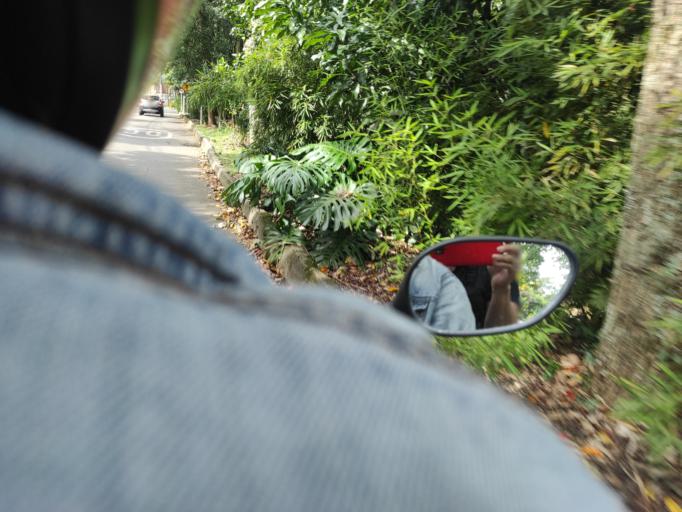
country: CO
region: Antioquia
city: Envigado
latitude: 6.1629
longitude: -75.5806
